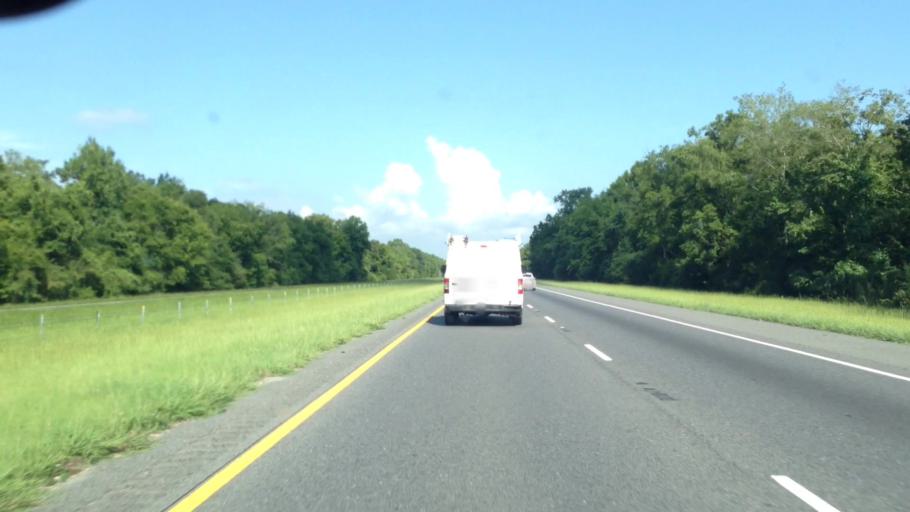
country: US
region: Louisiana
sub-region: Ascension Parish
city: Sorrento
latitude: 30.1592
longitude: -90.8317
